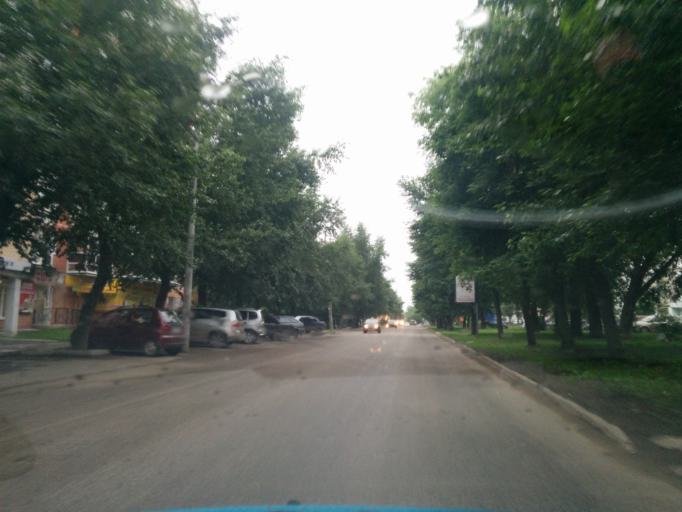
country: RU
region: Perm
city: Perm
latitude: 57.9960
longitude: 56.2266
